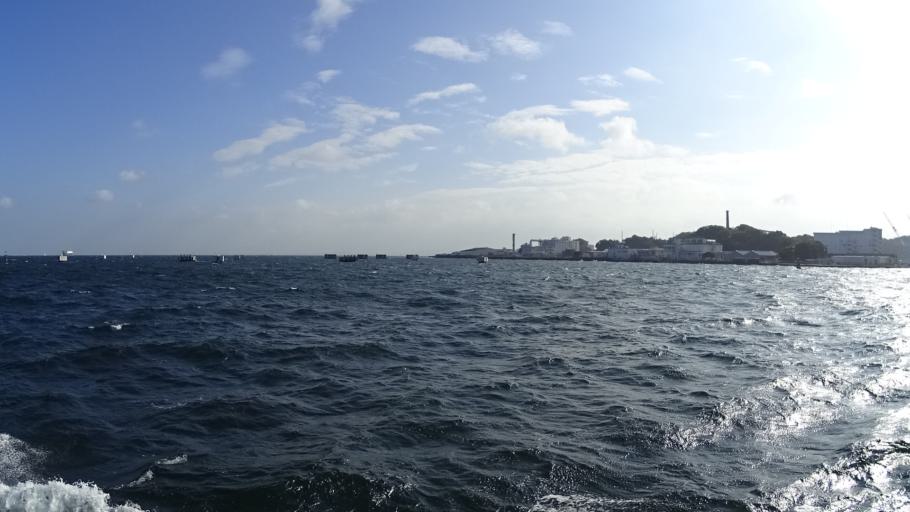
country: JP
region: Kanagawa
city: Yokosuka
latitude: 35.3032
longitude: 139.6595
